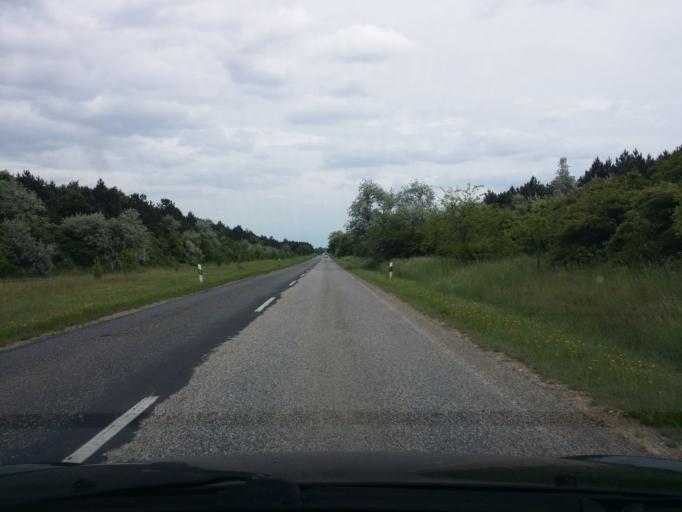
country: HU
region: Veszprem
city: Szentkiralyszabadja
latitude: 47.0641
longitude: 17.9563
